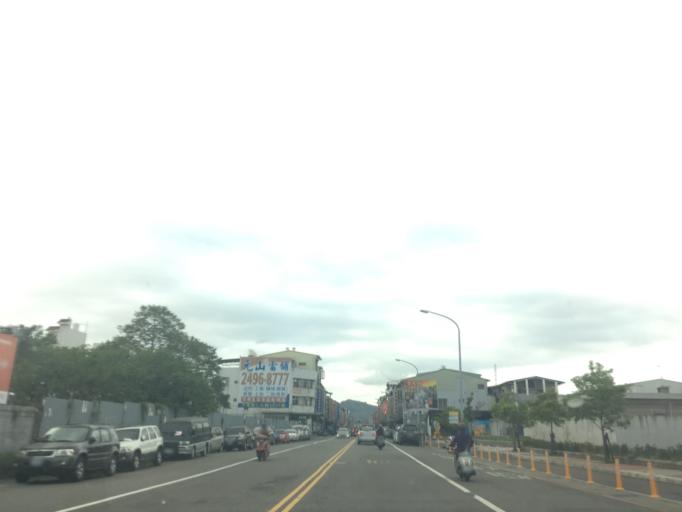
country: TW
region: Taiwan
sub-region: Taichung City
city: Taichung
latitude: 24.1513
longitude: 120.7332
